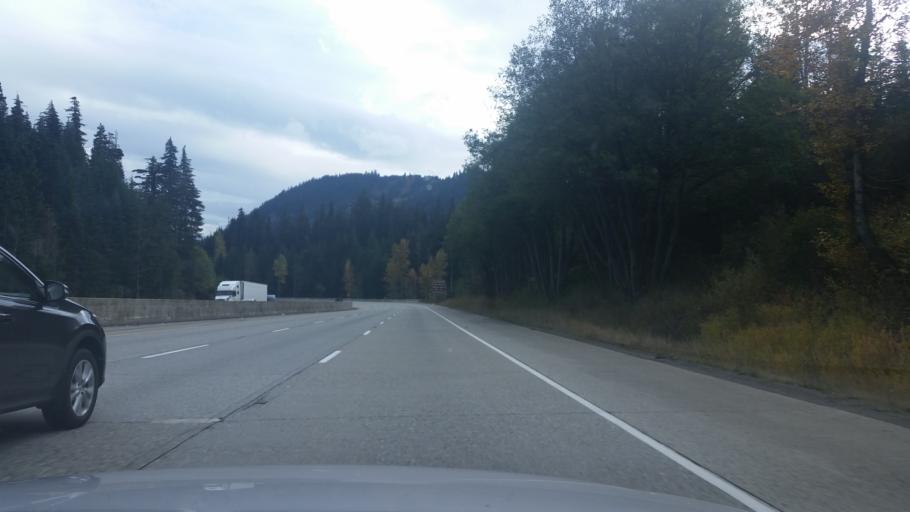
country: US
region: Washington
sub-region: King County
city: Tanner
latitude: 47.4047
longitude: -121.4044
